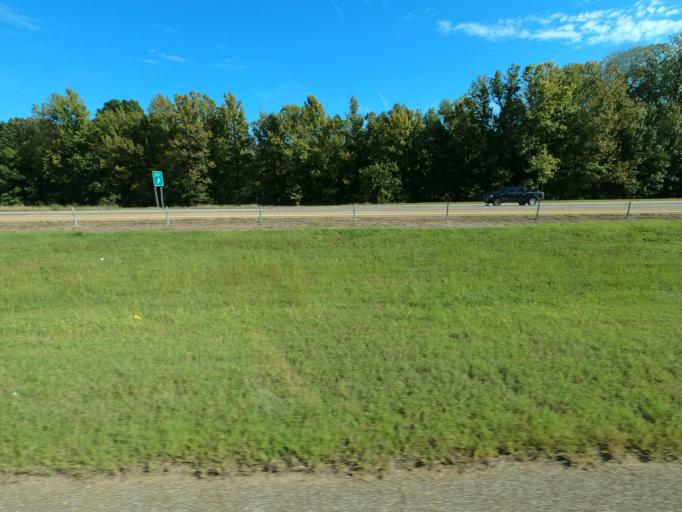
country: US
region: Tennessee
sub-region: Shelby County
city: Millington
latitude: 35.3169
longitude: -89.8697
